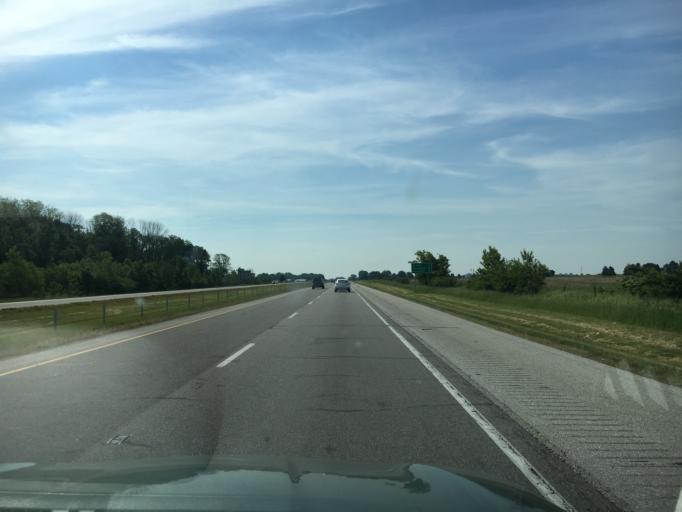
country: US
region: Indiana
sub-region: Decatur County
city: Saint Paul
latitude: 39.4902
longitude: -85.6858
